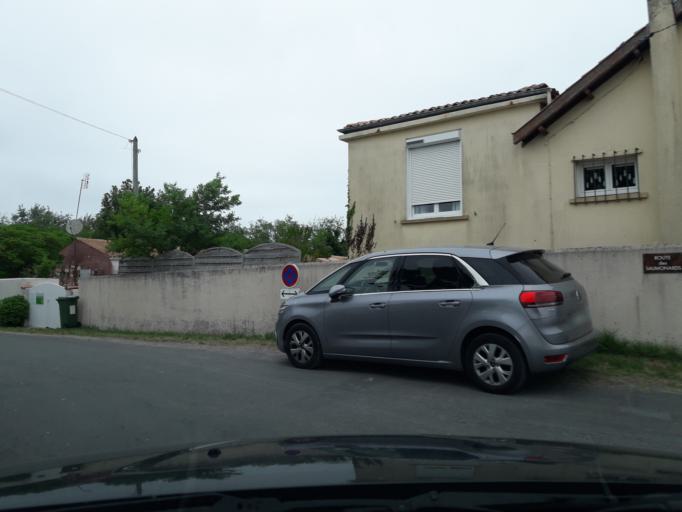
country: FR
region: Poitou-Charentes
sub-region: Departement de la Charente-Maritime
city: Boyard-Ville
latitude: 45.9691
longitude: -1.2382
